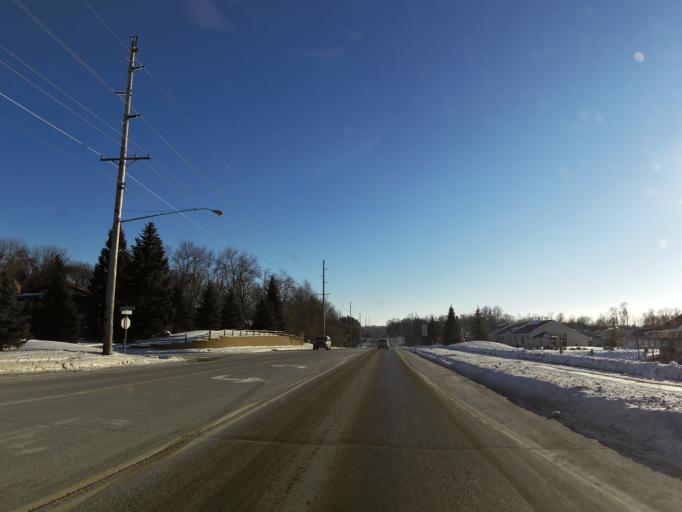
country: US
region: Minnesota
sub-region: Hennepin County
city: Mound
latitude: 44.9566
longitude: -93.6658
